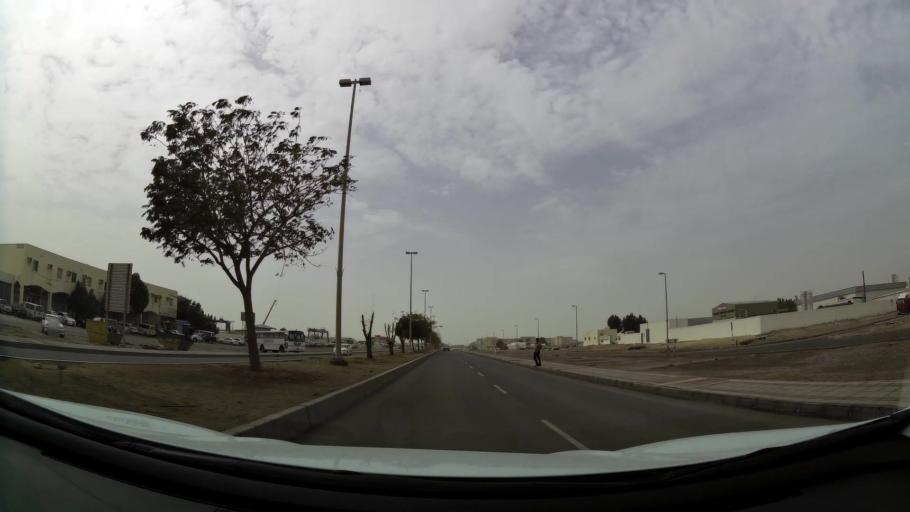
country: AE
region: Abu Dhabi
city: Abu Dhabi
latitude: 24.3538
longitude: 54.4782
